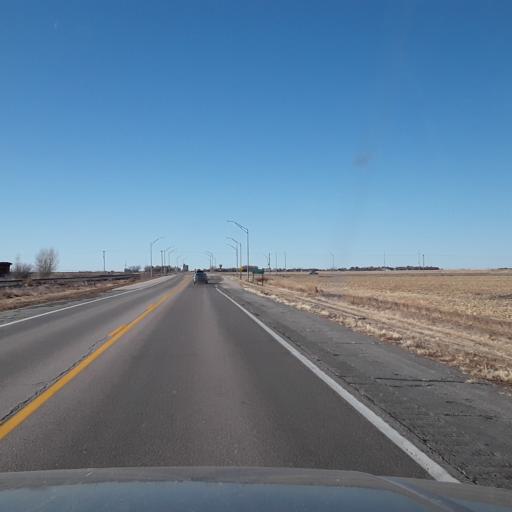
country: US
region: Nebraska
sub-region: Kearney County
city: Minden
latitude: 40.4847
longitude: -99.0804
